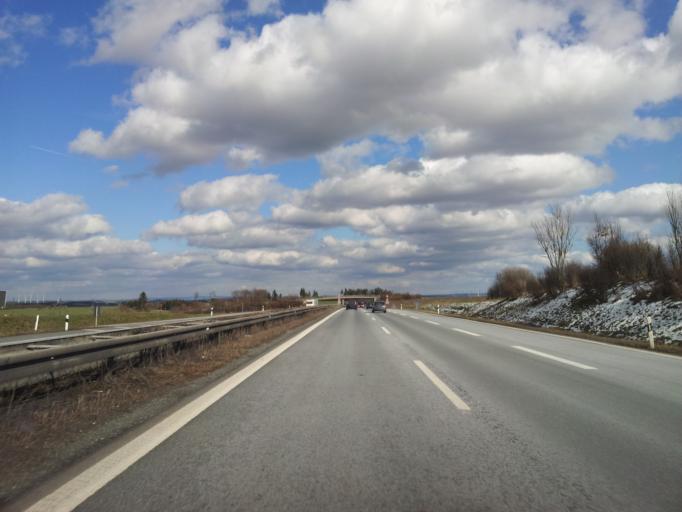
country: DE
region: Bavaria
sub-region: Upper Franconia
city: Koditz
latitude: 50.3429
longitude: 11.8323
